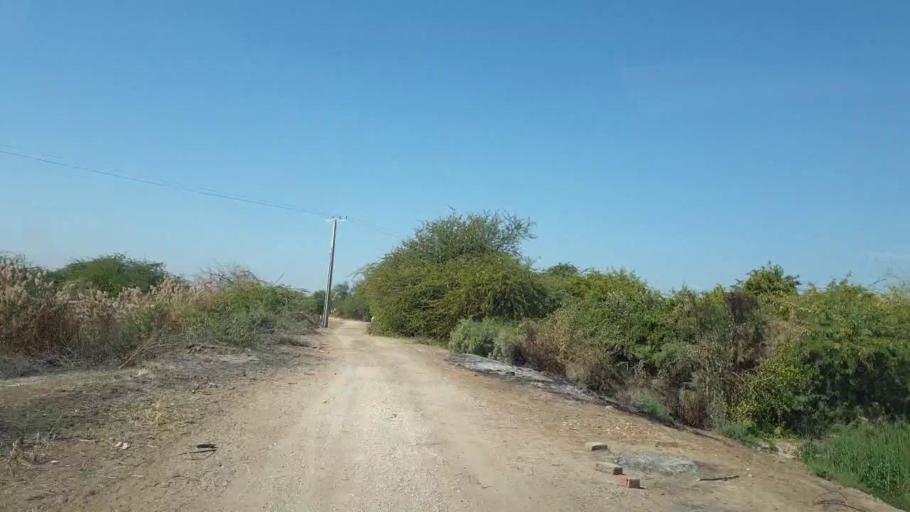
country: PK
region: Sindh
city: Mirpur Khas
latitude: 25.6150
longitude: 69.1371
